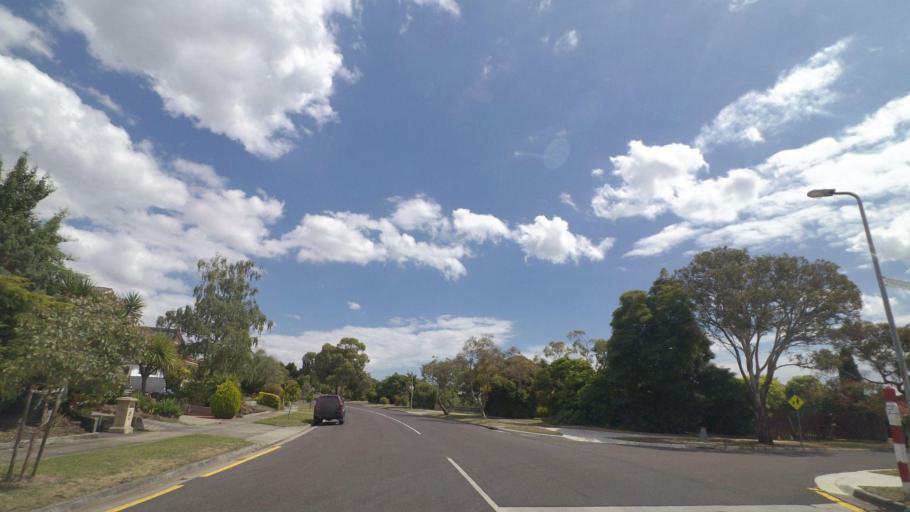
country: AU
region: Victoria
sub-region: Knox
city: Wantirna
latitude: -37.8573
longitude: 145.2185
